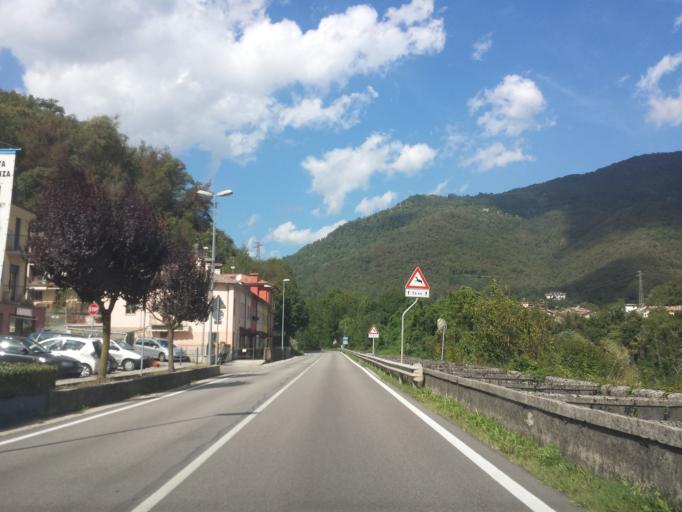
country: IT
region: Veneto
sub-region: Provincia di Vicenza
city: San Quirico
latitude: 45.6676
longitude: 11.2871
